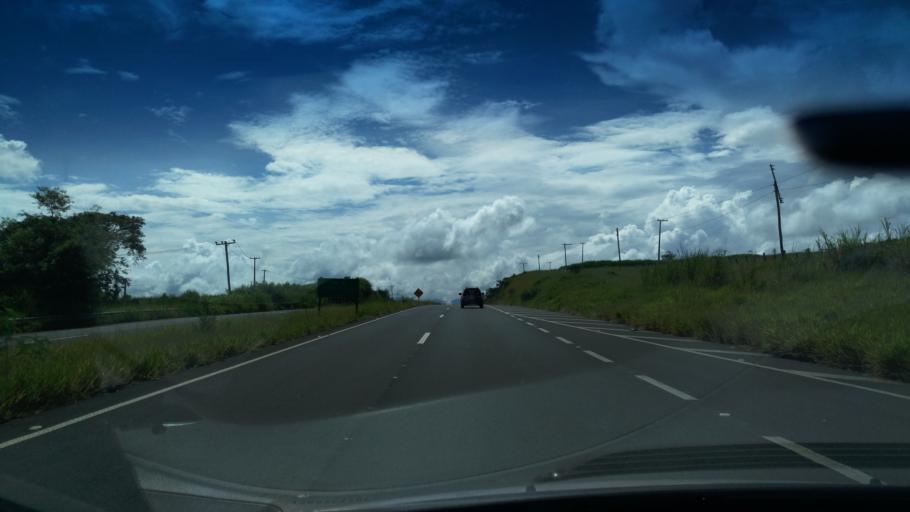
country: BR
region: Sao Paulo
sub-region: Santo Antonio Do Jardim
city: Espirito Santo do Pinhal
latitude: -22.1718
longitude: -46.7445
